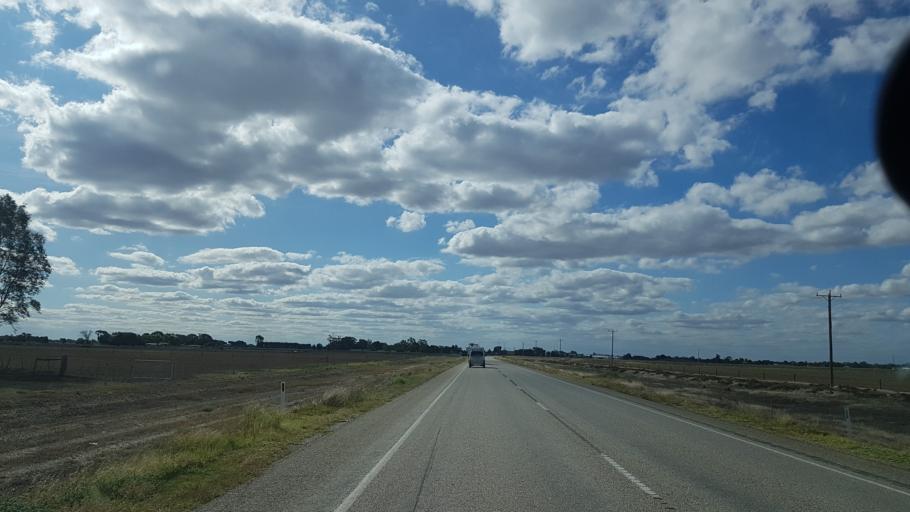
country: AU
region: Victoria
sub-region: Swan Hill
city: Swan Hill
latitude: -35.7683
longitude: 143.9335
